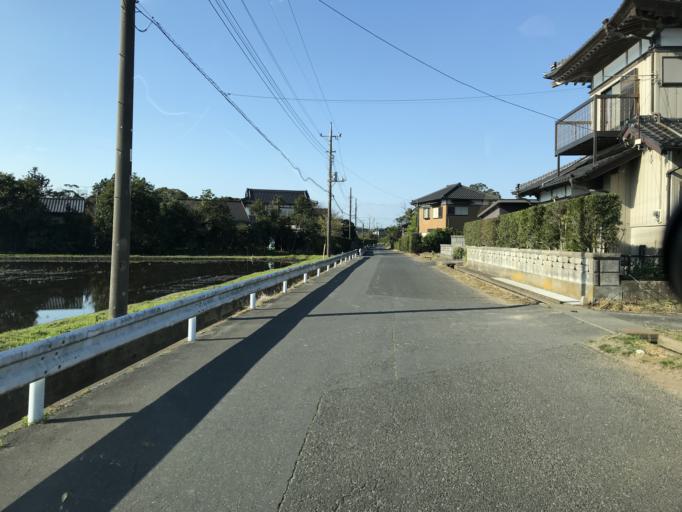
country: JP
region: Chiba
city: Omigawa
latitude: 35.8420
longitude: 140.6014
